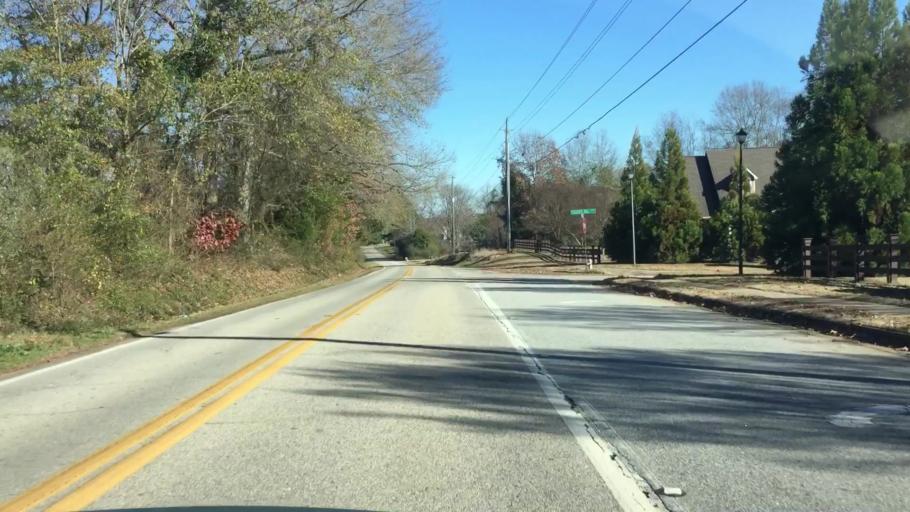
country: US
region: Georgia
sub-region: Newton County
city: Oakwood
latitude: 33.4677
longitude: -84.0062
